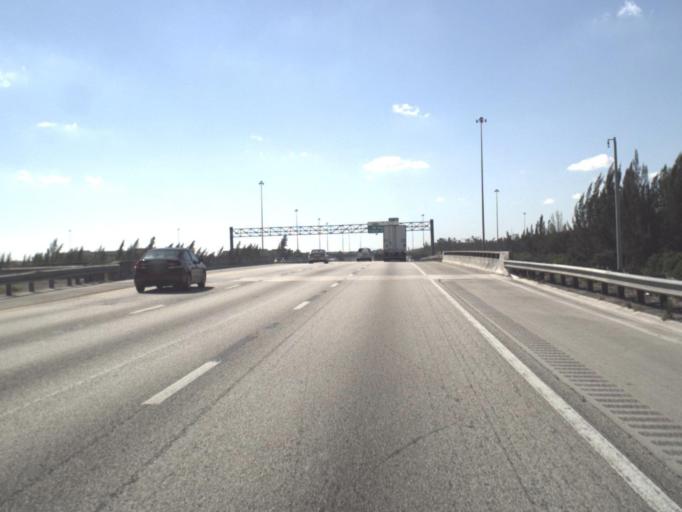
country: US
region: Florida
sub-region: Miami-Dade County
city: Hialeah Gardens
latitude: 25.8775
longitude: -80.3885
